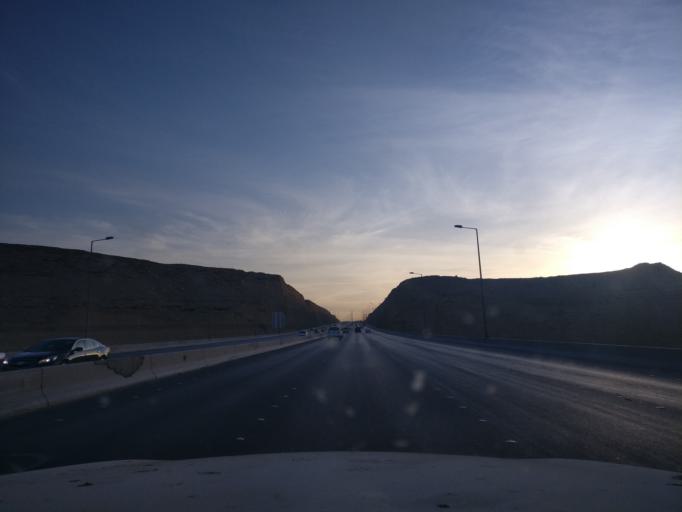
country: SA
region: Ar Riyad
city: Riyadh
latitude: 24.6124
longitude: 46.5654
